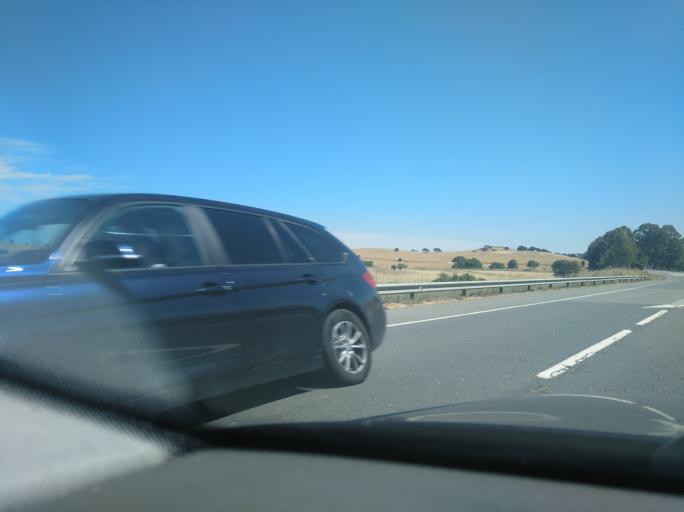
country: PT
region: Beja
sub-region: Castro Verde
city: Castro Verde
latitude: 37.6849
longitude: -8.0842
